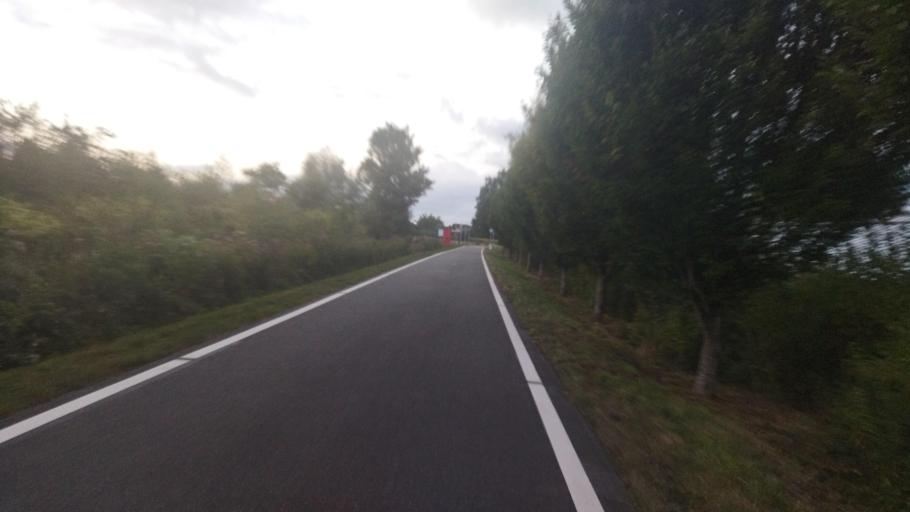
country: DE
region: North Rhine-Westphalia
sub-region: Regierungsbezirk Munster
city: Horstmar
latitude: 52.0783
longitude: 7.3209
